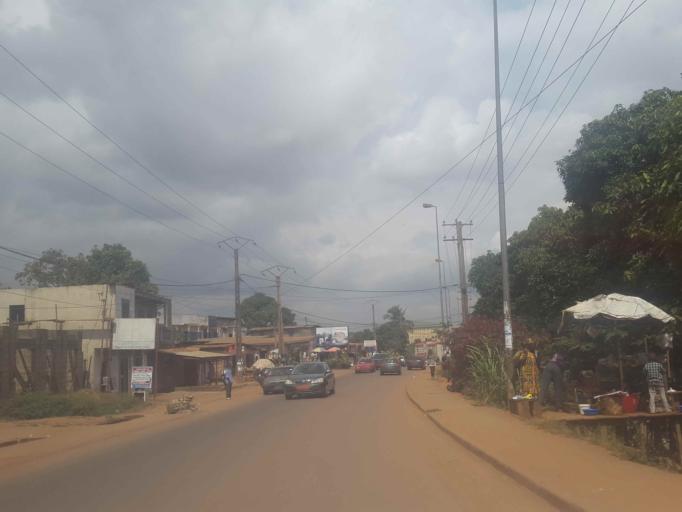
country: CM
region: Centre
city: Yaounde
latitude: 3.8734
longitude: 11.4787
